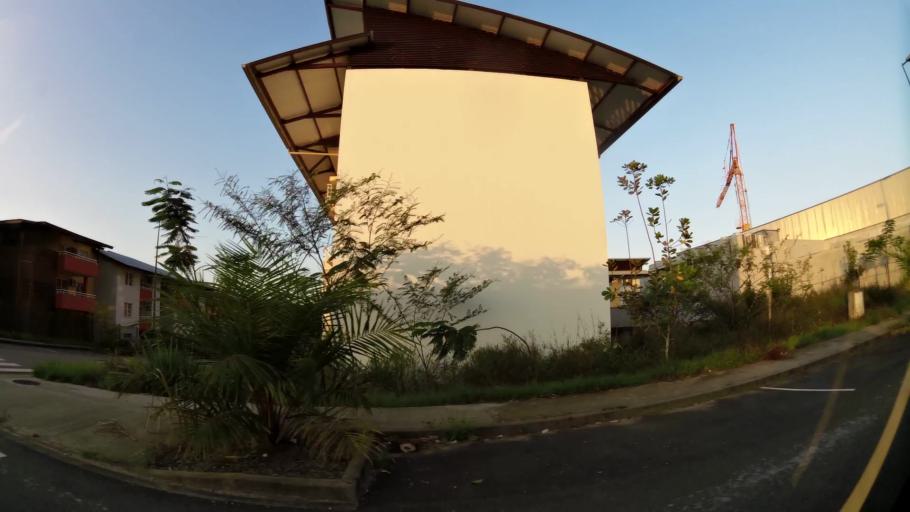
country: GF
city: Macouria
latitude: 4.9321
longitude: -52.4088
